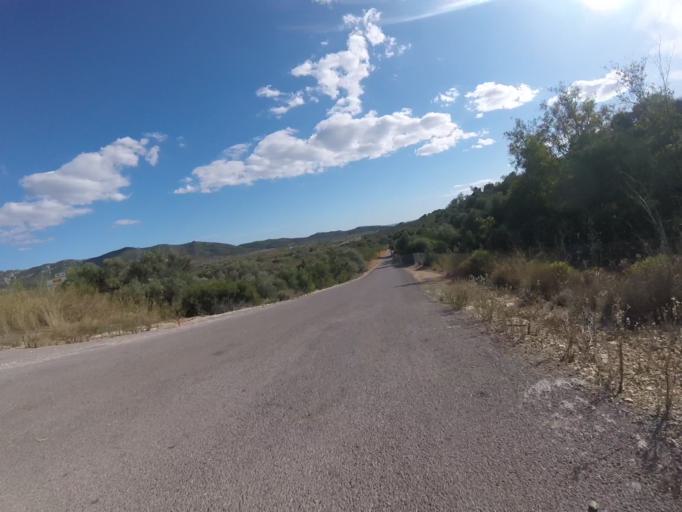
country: ES
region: Valencia
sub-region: Provincia de Castello
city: Alcala de Xivert
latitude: 40.2741
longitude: 0.2351
